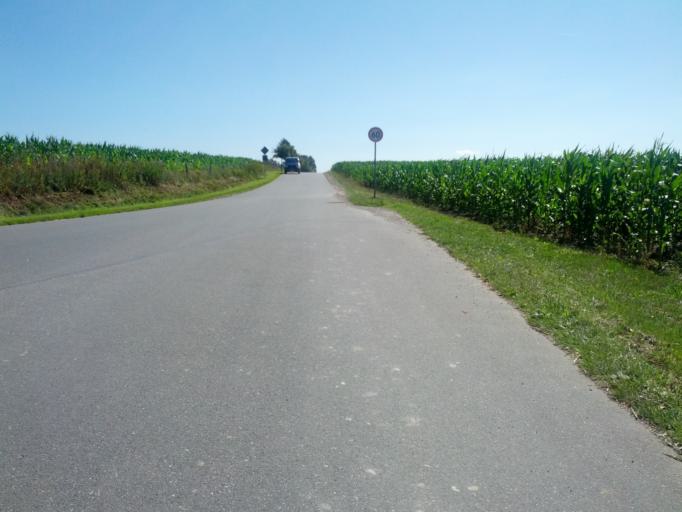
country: DE
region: Mecklenburg-Vorpommern
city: Bastorf
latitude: 54.1285
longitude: 11.6823
